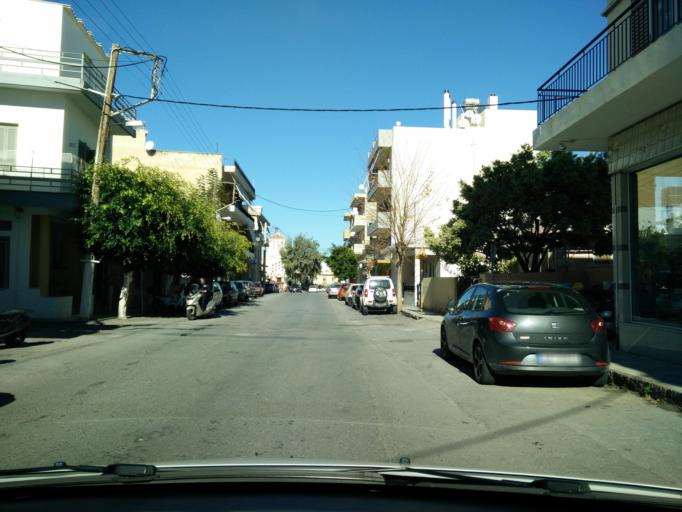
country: GR
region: Crete
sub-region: Nomos Irakleiou
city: Irakleion
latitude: 35.3350
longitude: 25.1465
